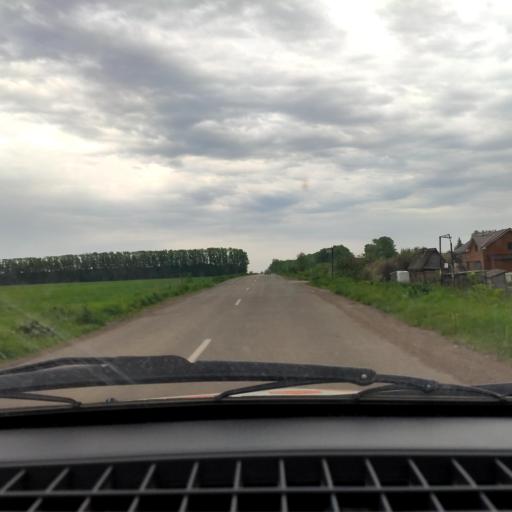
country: RU
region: Bashkortostan
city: Avdon
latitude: 54.5380
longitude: 55.7626
